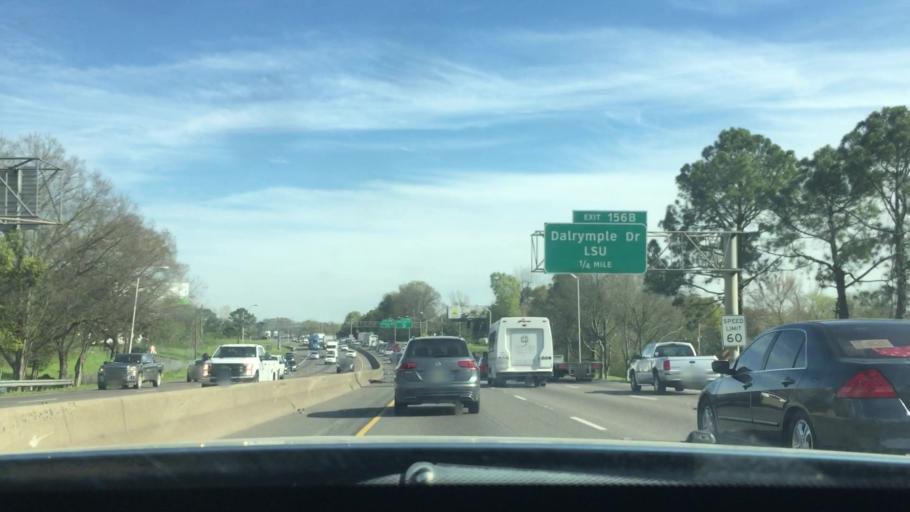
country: US
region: Louisiana
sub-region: East Baton Rouge Parish
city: Baton Rouge
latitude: 30.4299
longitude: -91.1732
